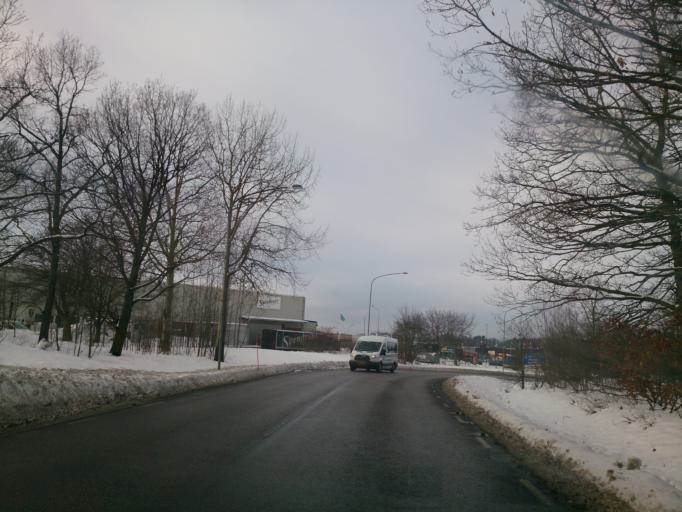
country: SE
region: OEstergoetland
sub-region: Norrkopings Kommun
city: Norrkoping
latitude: 58.6164
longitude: 16.1579
